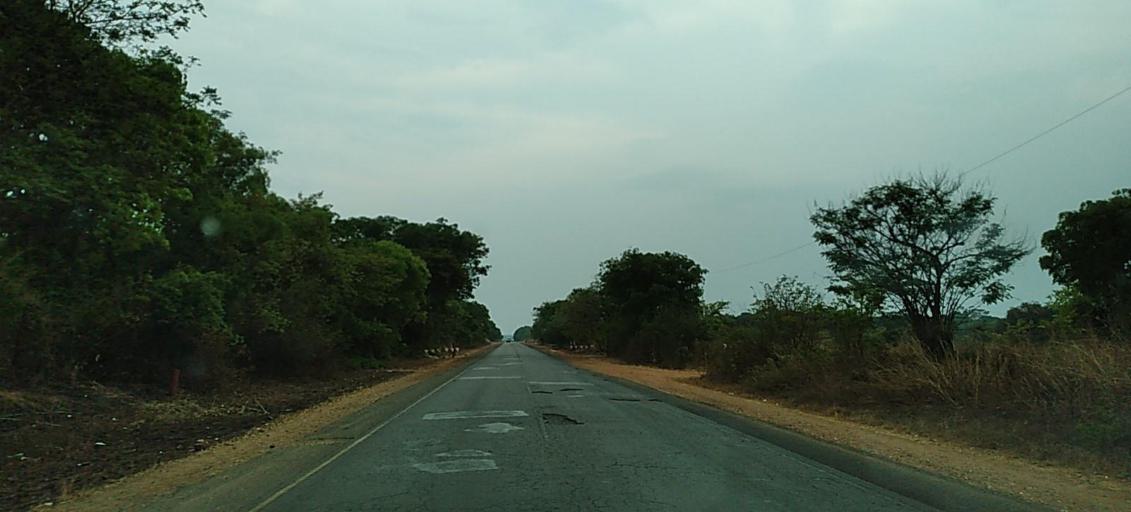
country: ZM
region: Copperbelt
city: Luanshya
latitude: -13.0665
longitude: 28.4534
